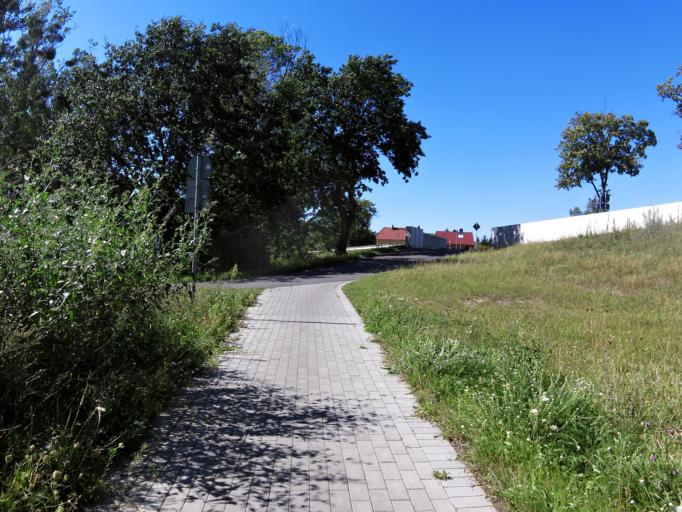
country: DE
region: Saxony-Anhalt
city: Elster
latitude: 51.8358
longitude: 12.7916
